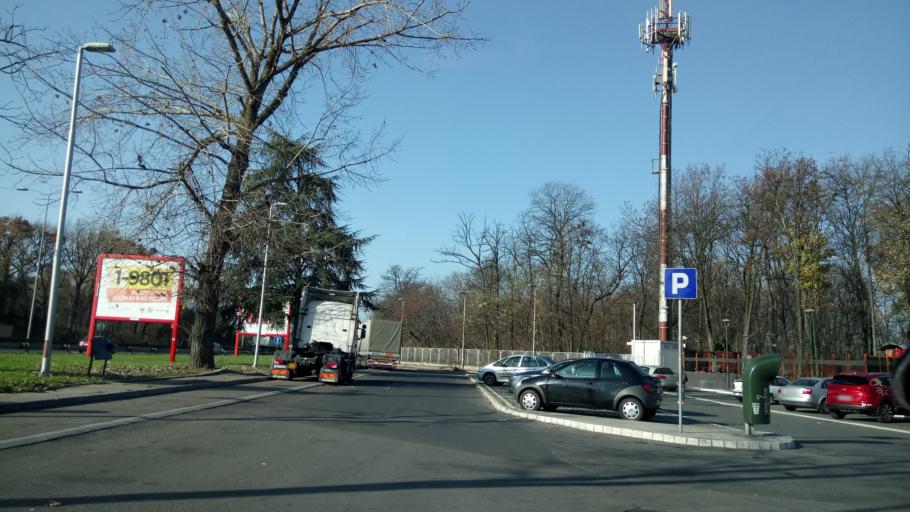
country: RS
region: Central Serbia
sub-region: Belgrade
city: Zemun
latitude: 44.8318
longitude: 20.3694
